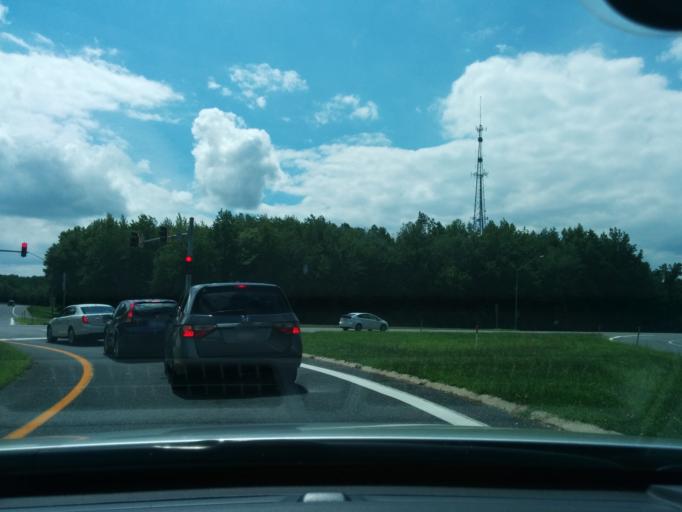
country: US
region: Maryland
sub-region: Worcester County
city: Ocean Pines
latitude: 38.3814
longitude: -75.1715
